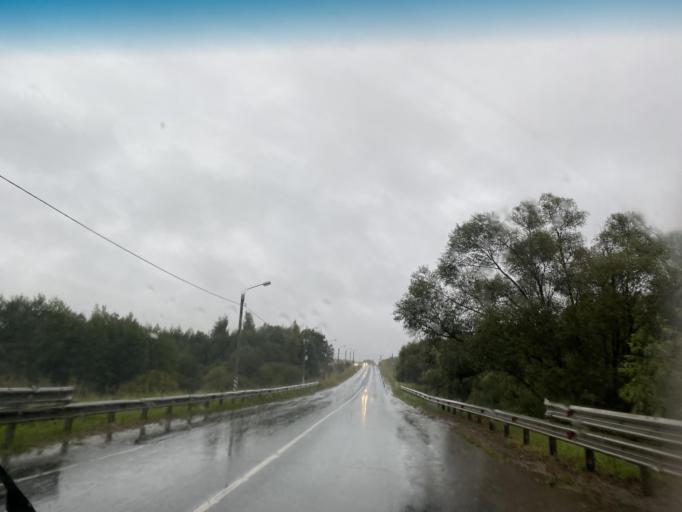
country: RU
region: Rjazan
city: Starozhilovo
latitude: 54.3805
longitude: 39.9255
